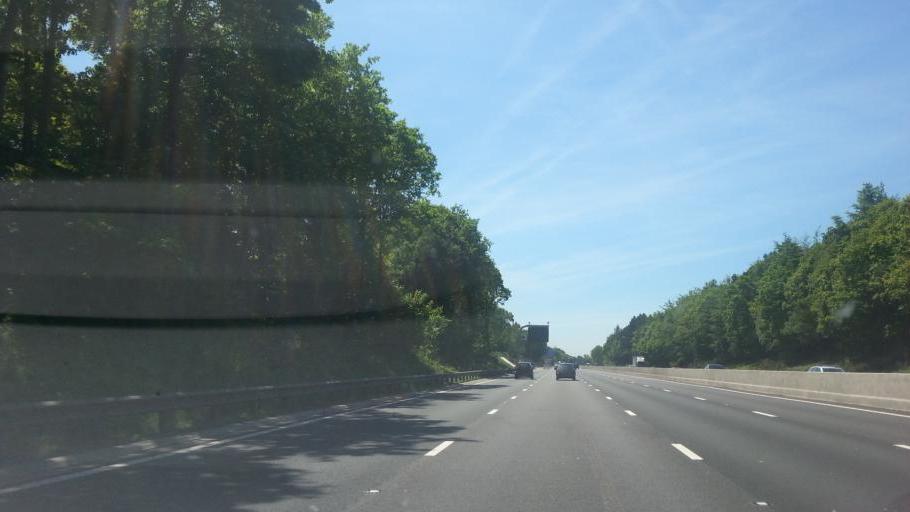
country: GB
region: England
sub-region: Surrey
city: Camberley
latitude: 51.3298
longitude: -0.7290
